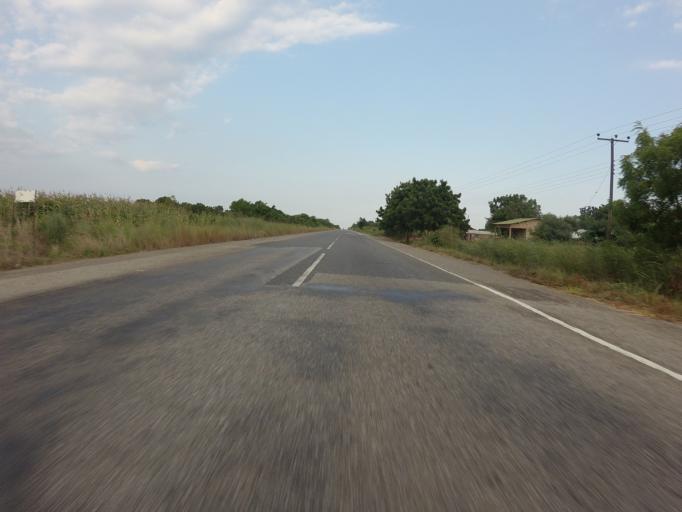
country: GH
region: Volta
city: Anloga
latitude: 6.0866
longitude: 0.5477
